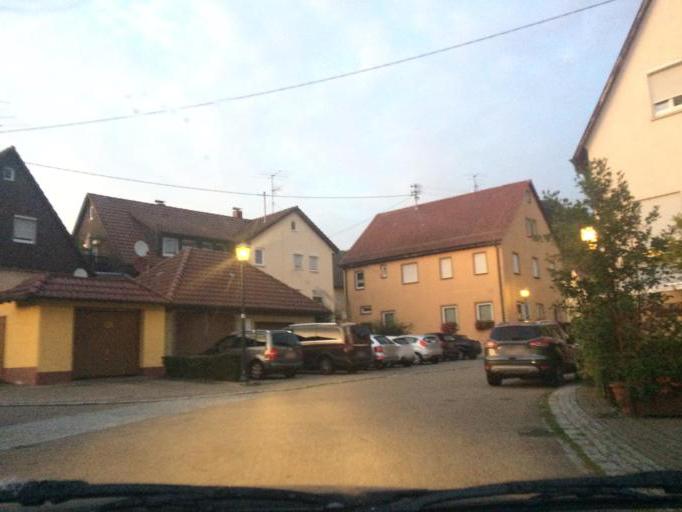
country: DE
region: Baden-Wuerttemberg
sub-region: Regierungsbezirk Stuttgart
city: Schorndorf
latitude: 48.8308
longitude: 9.5110
